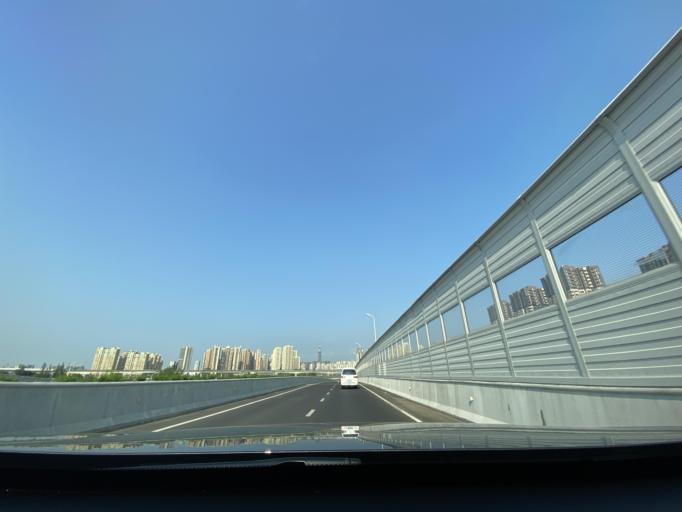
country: CN
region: Sichuan
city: Chengdu
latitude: 30.5982
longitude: 104.1078
